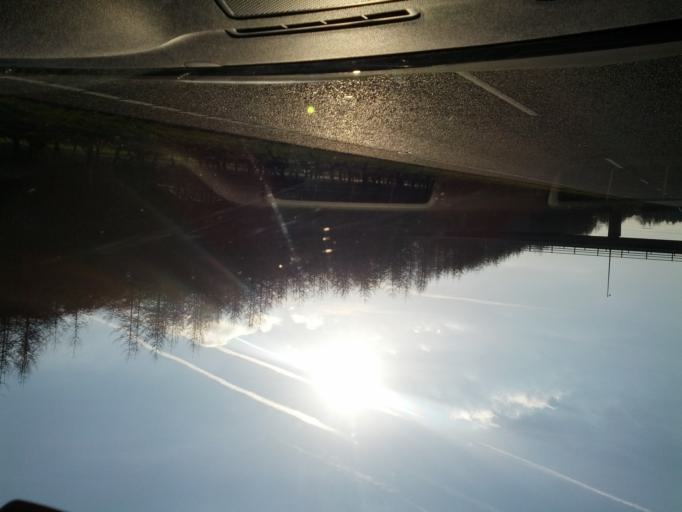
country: IE
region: Leinster
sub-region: Laois
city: Portlaoise
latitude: 53.0629
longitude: -7.2228
